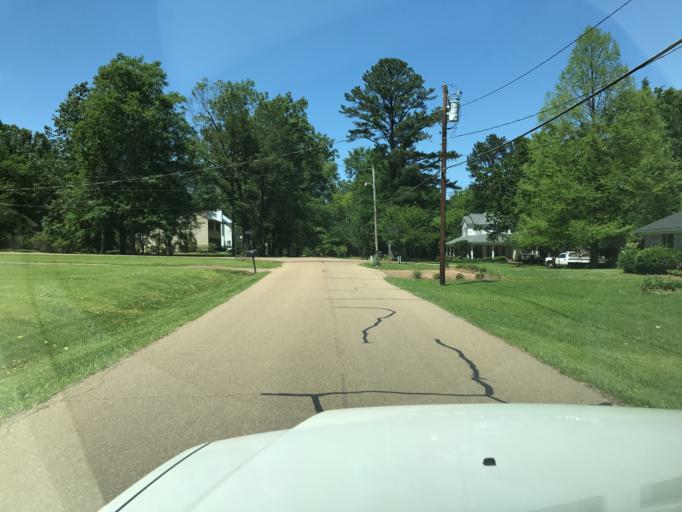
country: US
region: Mississippi
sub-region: Madison County
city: Ridgeland
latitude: 32.4296
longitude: -90.1336
